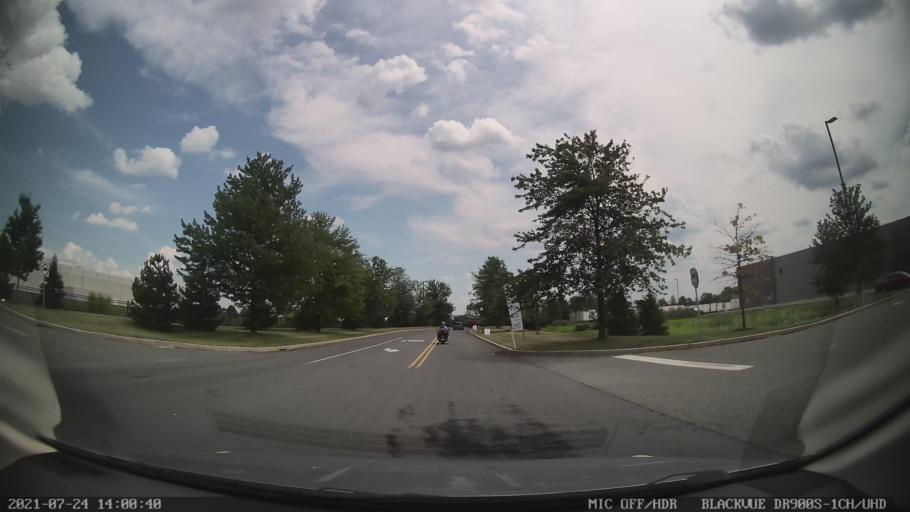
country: US
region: Pennsylvania
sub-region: Lehigh County
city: Trexlertown
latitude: 40.5699
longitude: -75.6222
